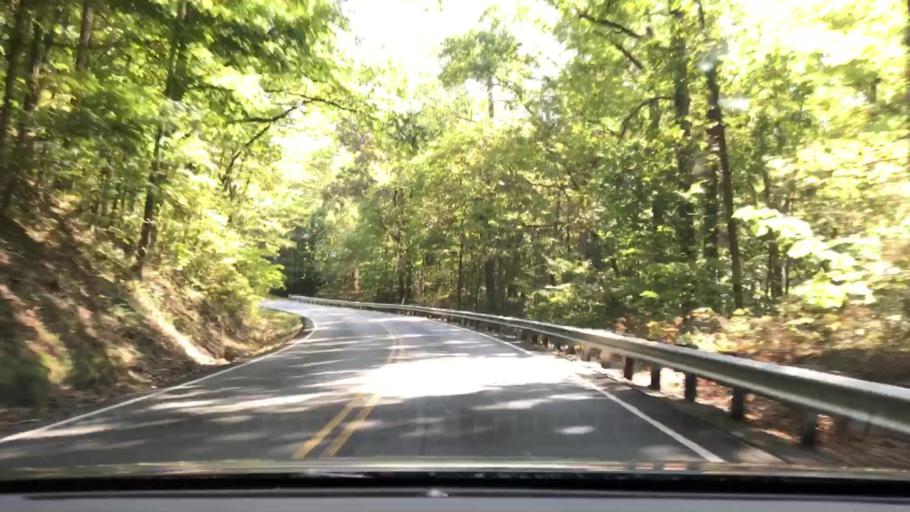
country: US
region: Kentucky
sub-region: Marshall County
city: Benton
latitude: 36.7656
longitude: -88.2704
